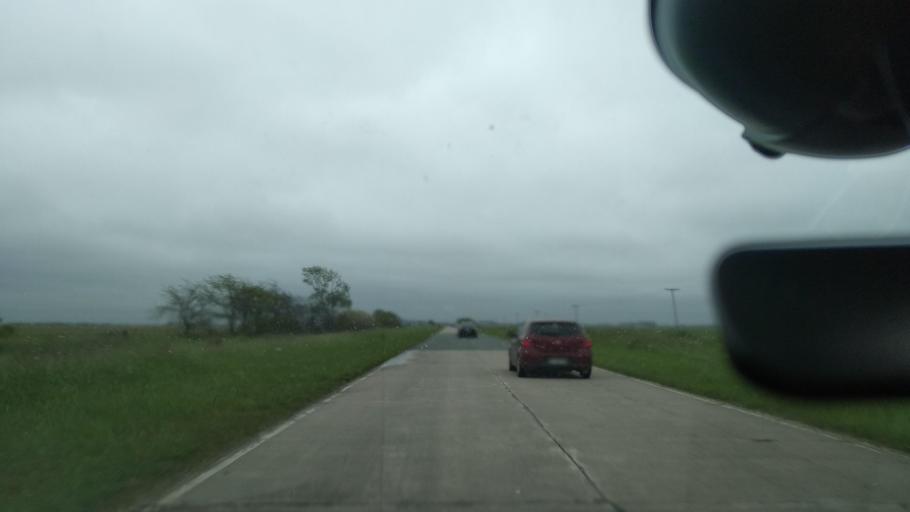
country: AR
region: Buenos Aires
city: Veronica
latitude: -35.5681
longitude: -57.2898
